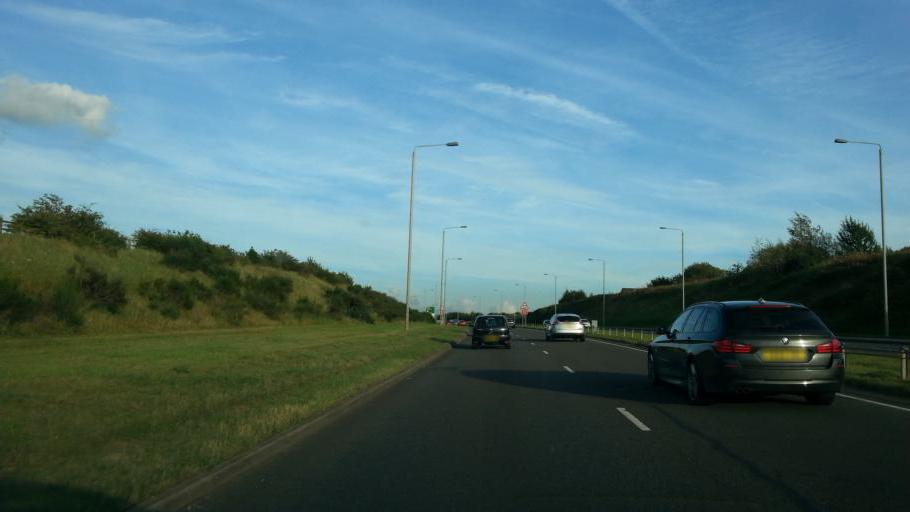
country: GB
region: England
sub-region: Nottinghamshire
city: Rainworth
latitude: 53.1211
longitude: -1.1117
